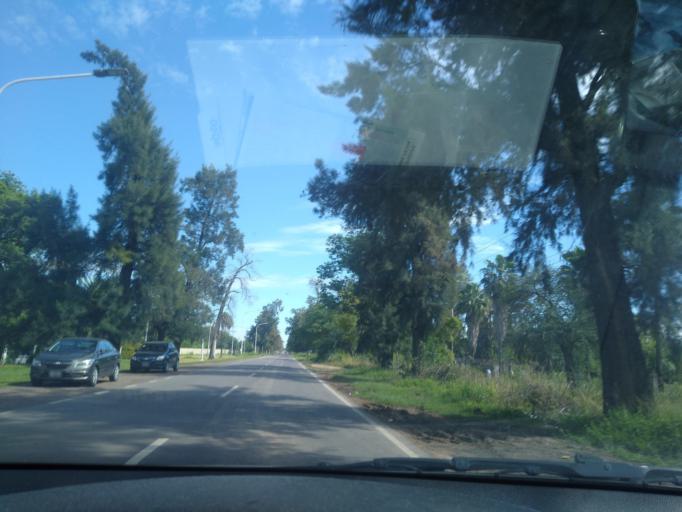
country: AR
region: Chaco
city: Presidencia Roque Saenz Pena
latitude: -26.7775
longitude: -60.4053
